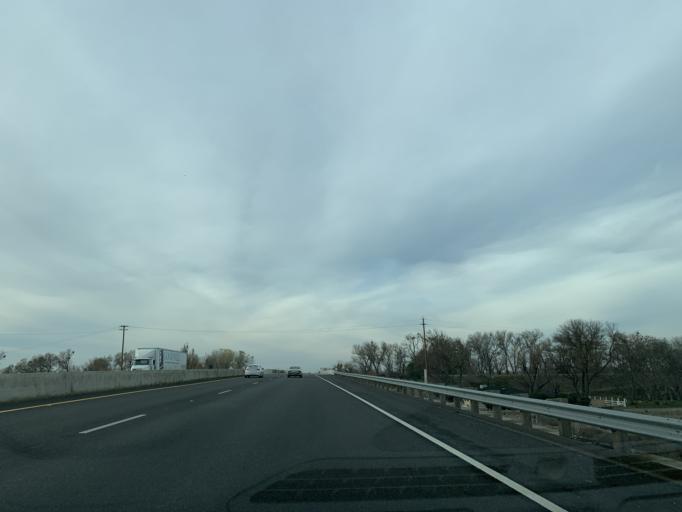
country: US
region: California
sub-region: Yuba County
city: Plumas Lake
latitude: 38.8982
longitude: -121.5831
